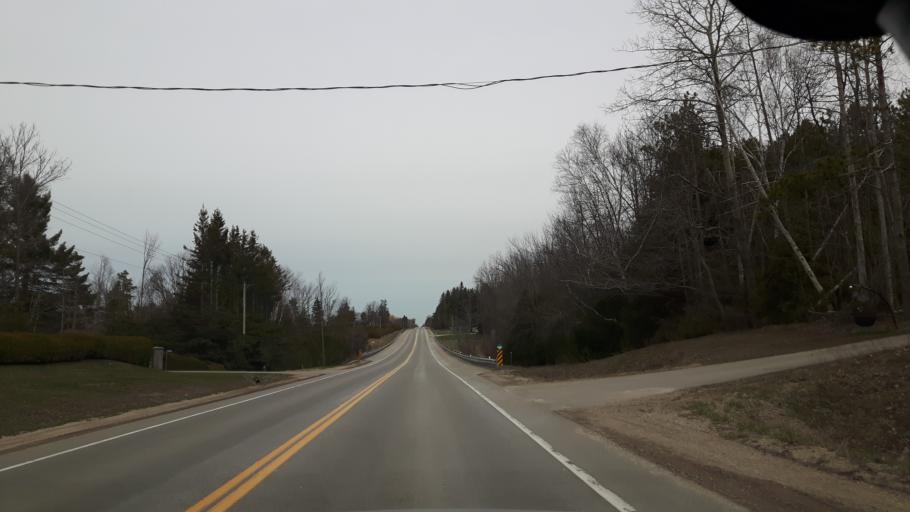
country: CA
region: Ontario
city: Goderich
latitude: 43.6649
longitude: -81.7056
